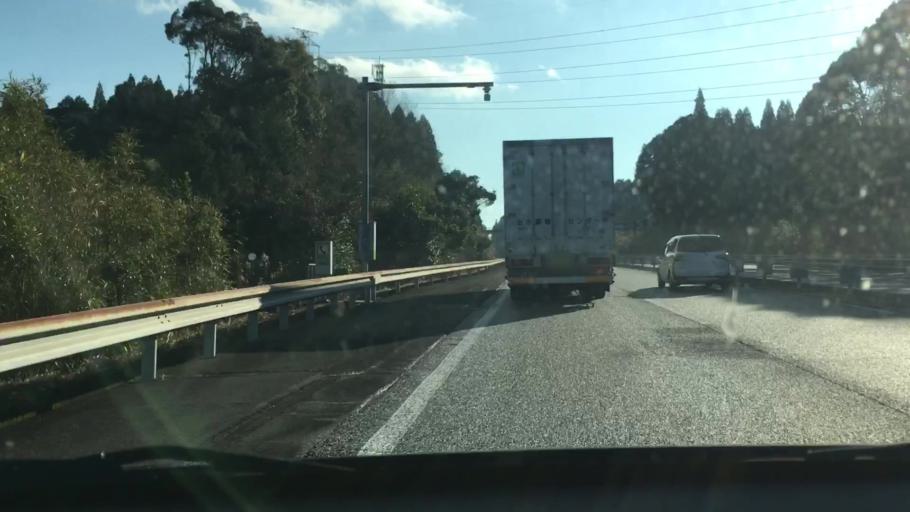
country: JP
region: Kagoshima
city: Okuchi-shinohara
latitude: 31.9310
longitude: 130.7056
